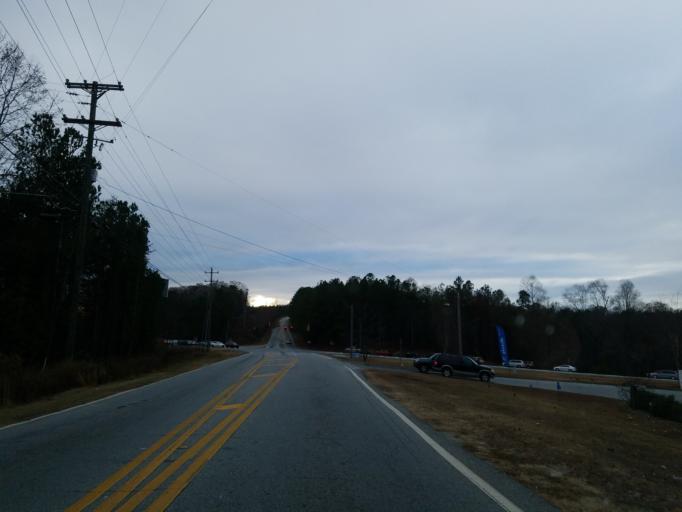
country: US
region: Georgia
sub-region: Dawson County
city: Dawsonville
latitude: 34.3799
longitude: -84.0227
